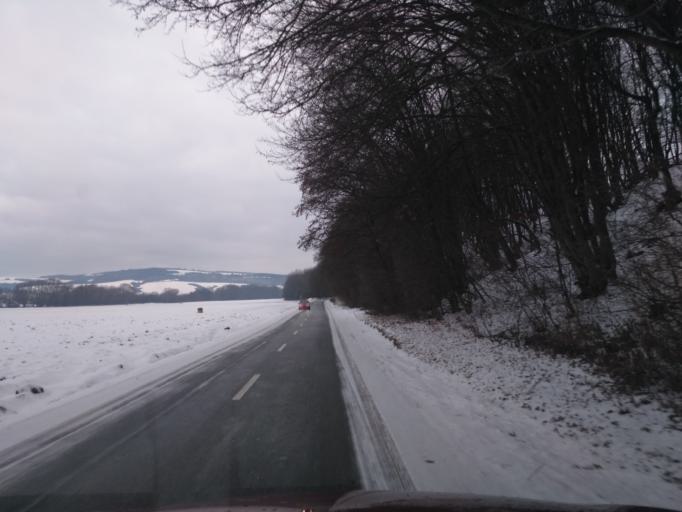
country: SK
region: Presovsky
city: Sabinov
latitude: 49.0522
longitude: 21.0895
